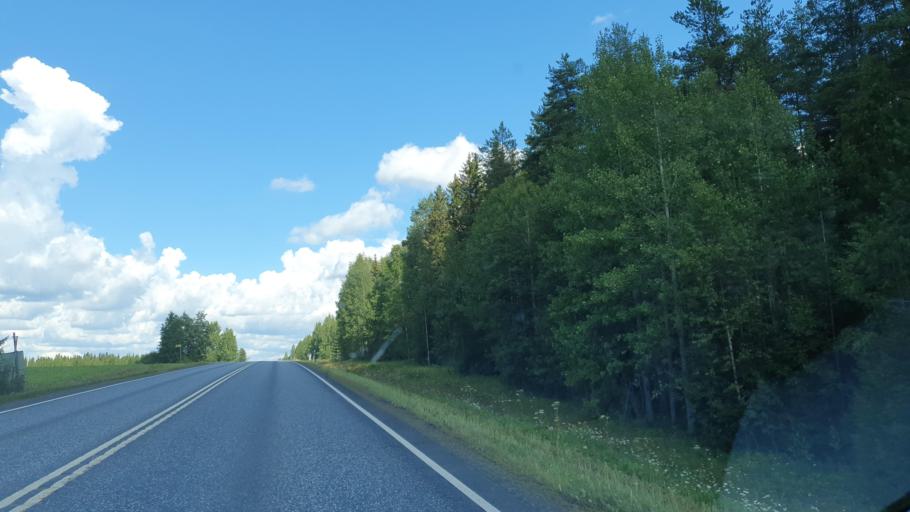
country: FI
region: Northern Savo
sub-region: Ylae-Savo
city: Sonkajaervi
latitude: 63.8073
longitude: 27.4181
